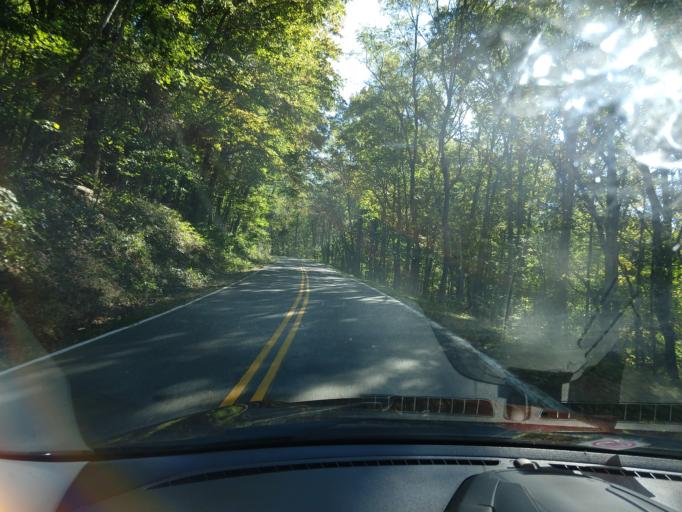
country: US
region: Virginia
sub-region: Alleghany County
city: Clifton Forge
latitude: 37.8885
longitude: -79.8863
